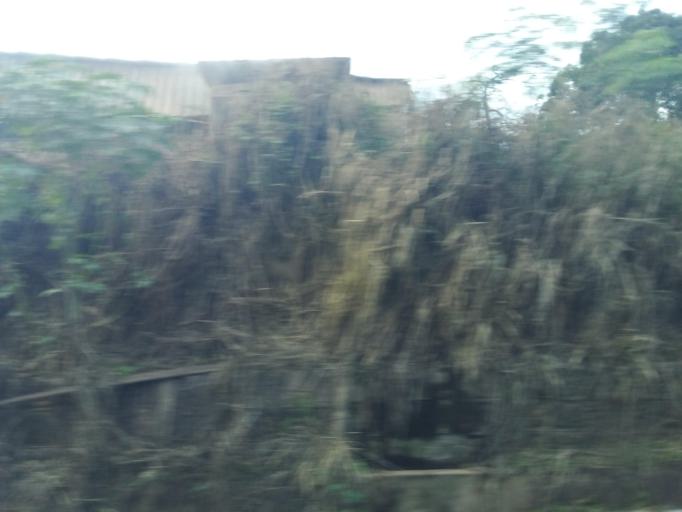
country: BR
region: Minas Gerais
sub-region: Governador Valadares
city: Governador Valadares
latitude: -18.9166
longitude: -42.0101
